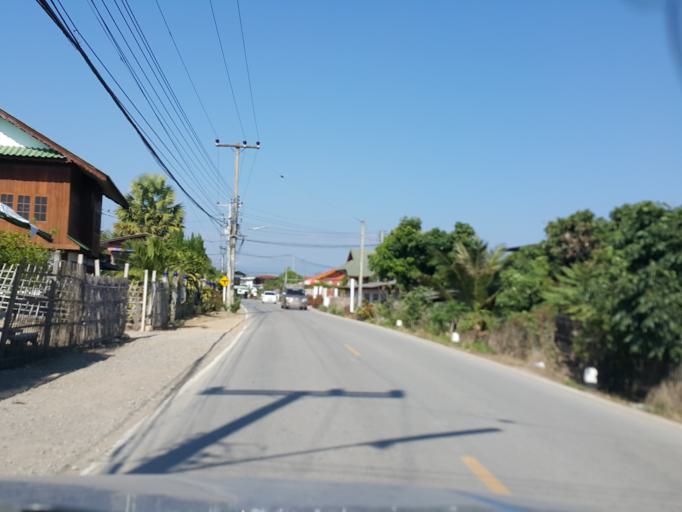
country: TH
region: Chiang Mai
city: Mae Wang
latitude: 18.5987
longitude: 98.8021
